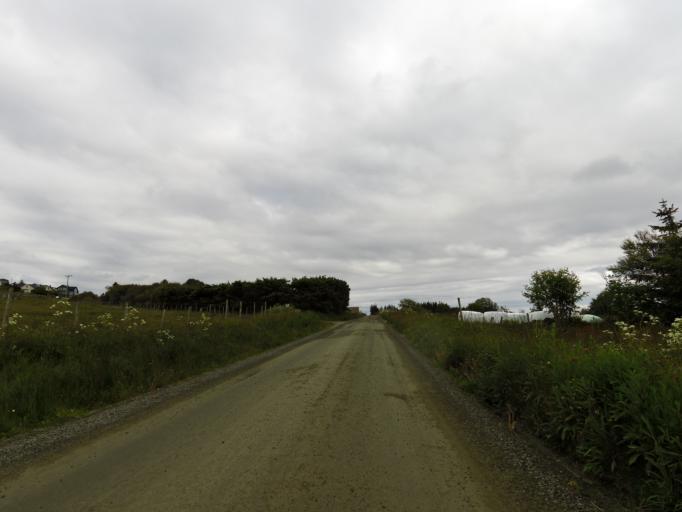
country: NO
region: Vest-Agder
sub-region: Farsund
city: Vestbygd
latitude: 58.1305
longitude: 6.6112
